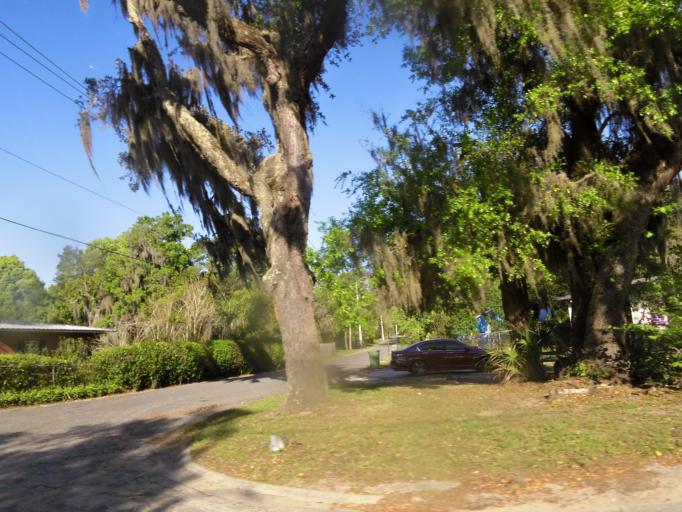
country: US
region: Florida
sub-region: Putnam County
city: Palatka
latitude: 29.6472
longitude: -81.6560
